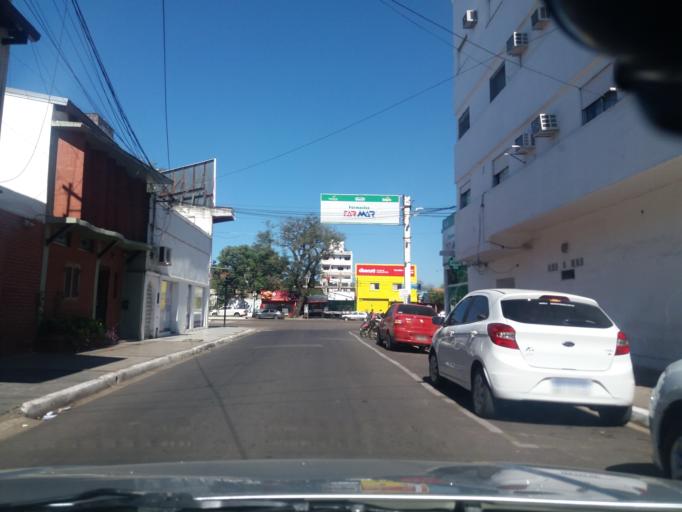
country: AR
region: Corrientes
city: Corrientes
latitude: -27.4748
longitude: -58.8396
